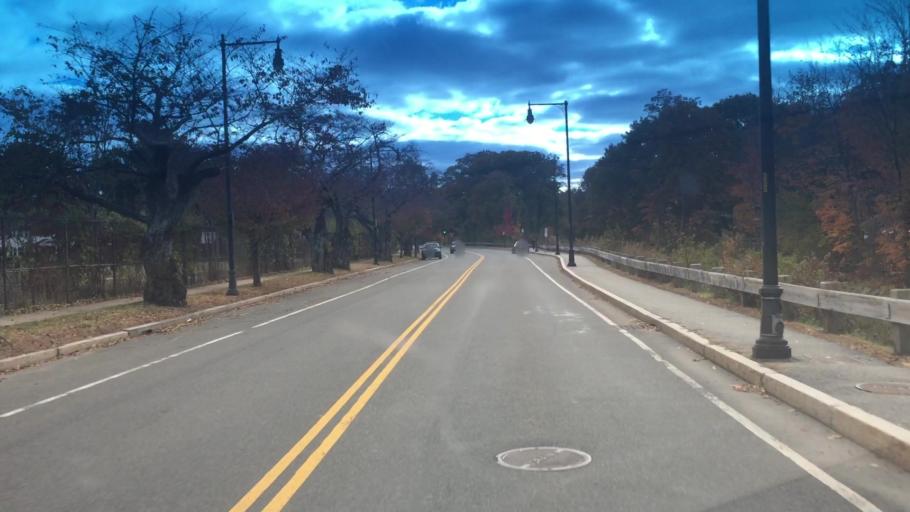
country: US
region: Massachusetts
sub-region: Middlesex County
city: Winchester
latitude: 42.4494
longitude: -71.1377
